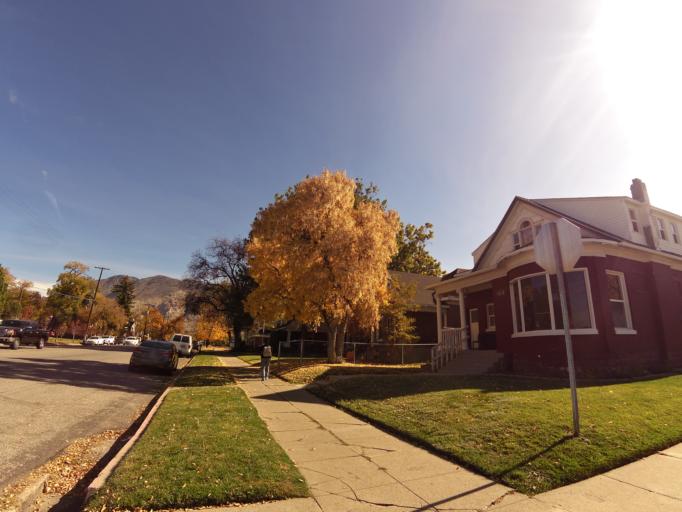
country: US
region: Utah
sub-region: Weber County
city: Ogden
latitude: 41.2204
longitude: -111.9635
